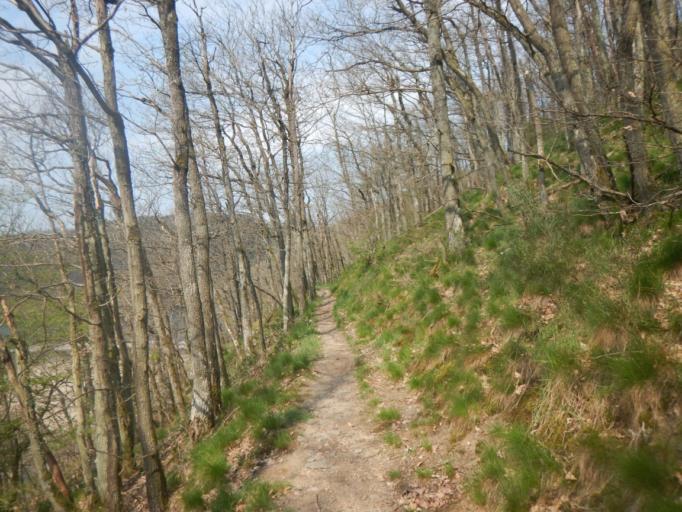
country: LU
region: Diekirch
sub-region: Canton de Wiltz
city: Esch-sur-Sure
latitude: 49.9109
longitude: 5.9262
